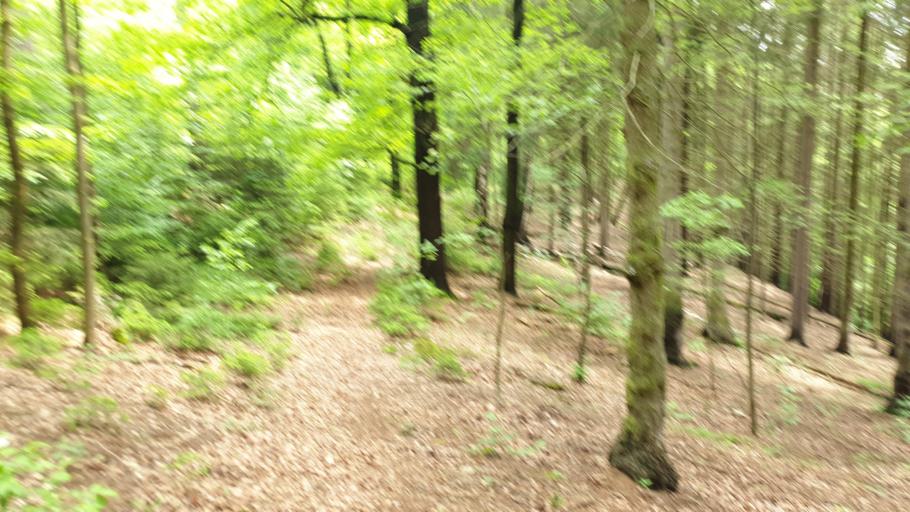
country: DE
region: Saxony
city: Gornau
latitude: 50.7840
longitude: 12.9739
